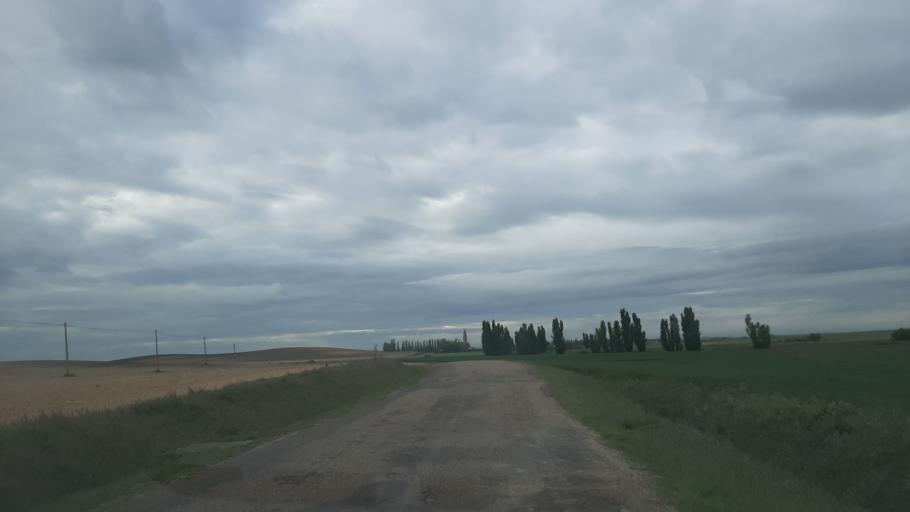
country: ES
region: Castille and Leon
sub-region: Provincia de Salamanca
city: Palaciosrubios
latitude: 41.0643
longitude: -5.2020
